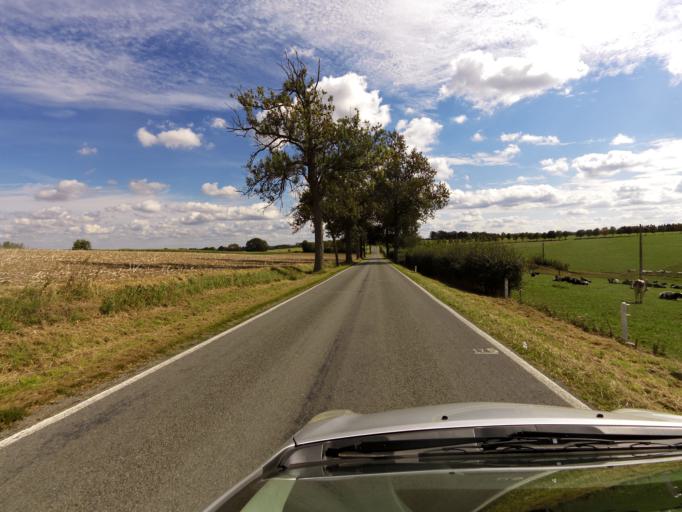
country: BE
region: Wallonia
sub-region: Province de Namur
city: Somme-Leuze
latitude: 50.3537
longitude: 5.3262
